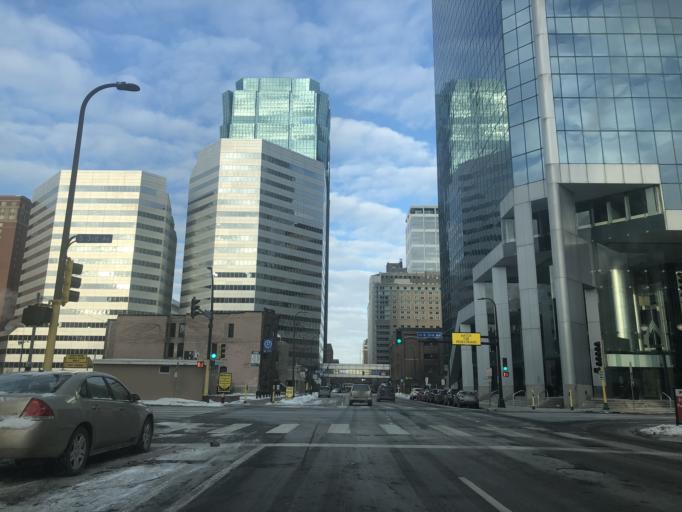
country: US
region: Minnesota
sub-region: Hennepin County
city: Minneapolis
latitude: 44.9731
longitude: -93.2695
